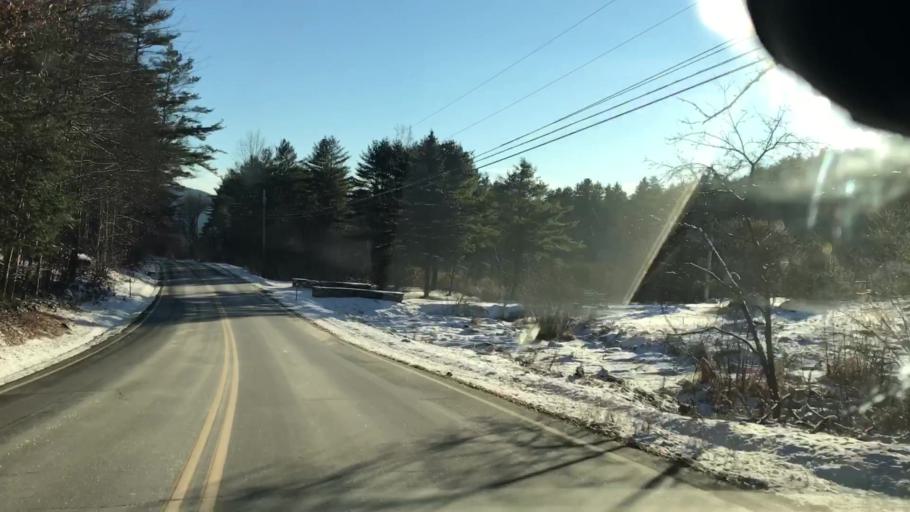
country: US
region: New Hampshire
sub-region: Grafton County
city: Haverhill
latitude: 43.9839
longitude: -72.0808
